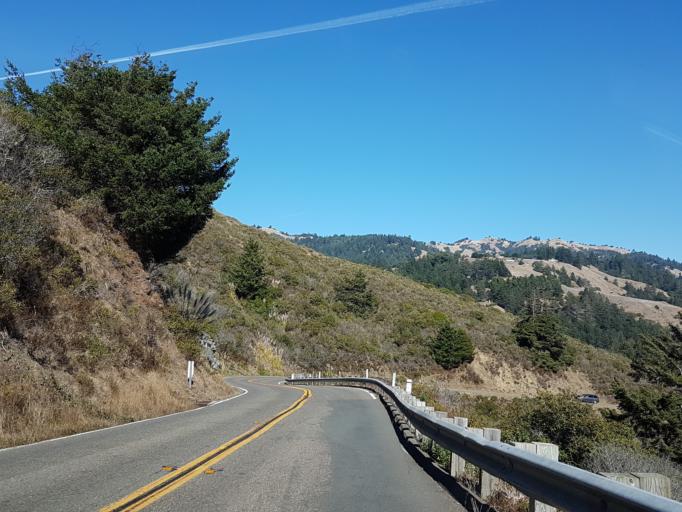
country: US
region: California
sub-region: Sonoma County
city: Monte Rio
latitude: 38.4739
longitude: -123.1568
